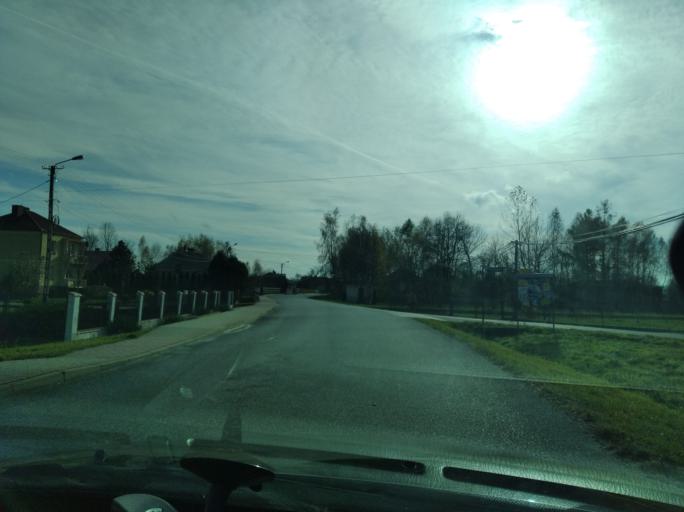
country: PL
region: Subcarpathian Voivodeship
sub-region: Powiat ropczycko-sedziszowski
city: Sedziszow Malopolski
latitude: 50.0820
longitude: 21.6978
